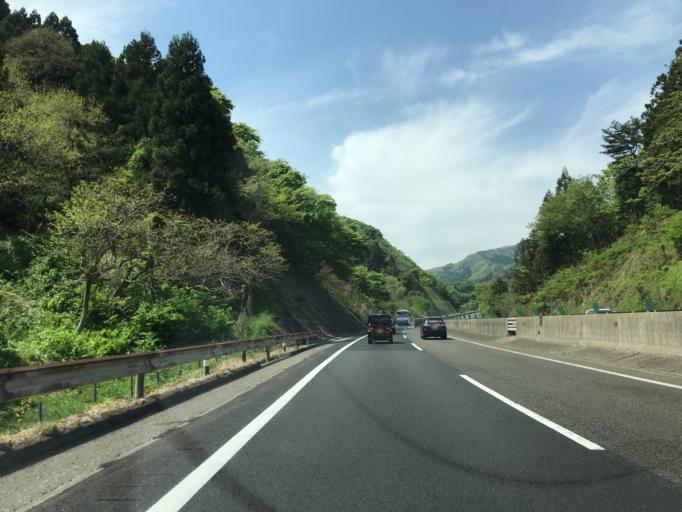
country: JP
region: Fukushima
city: Yanagawamachi-saiwaicho
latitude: 37.9116
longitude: 140.5970
